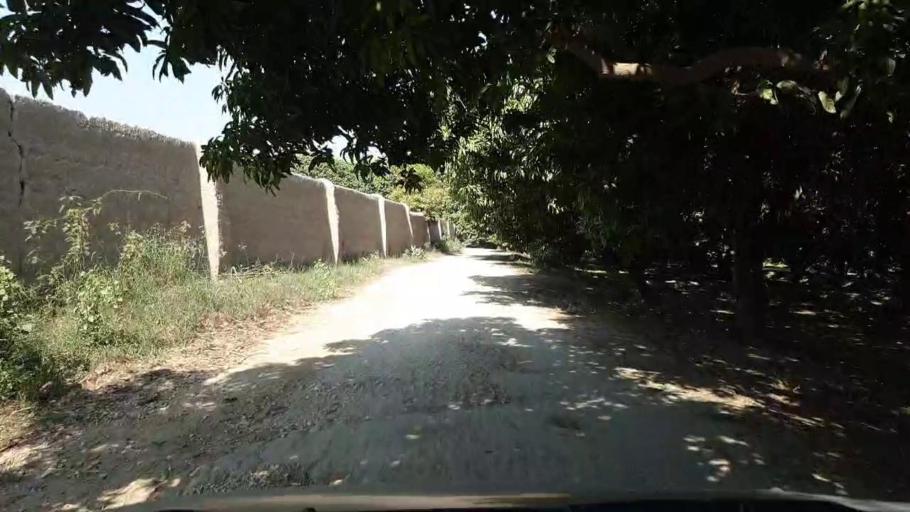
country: PK
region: Sindh
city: Tando Jam
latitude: 25.4026
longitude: 68.6310
